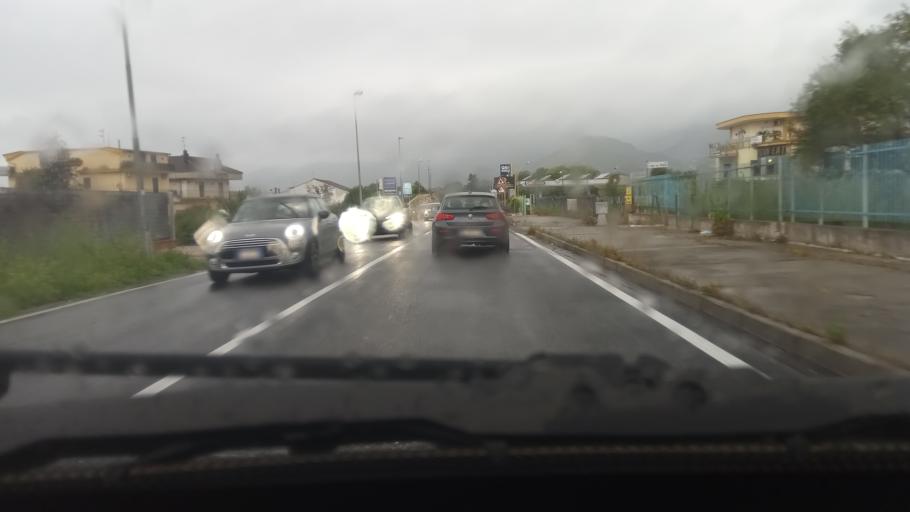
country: IT
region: Latium
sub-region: Provincia di Latina
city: Penitro
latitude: 41.2621
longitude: 13.6842
